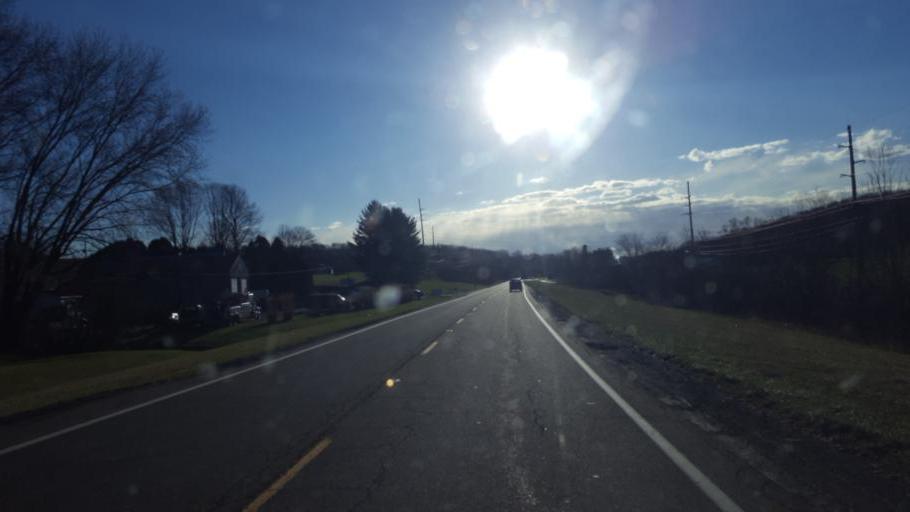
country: US
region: Ohio
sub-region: Holmes County
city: Millersburg
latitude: 40.5699
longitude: -81.9695
